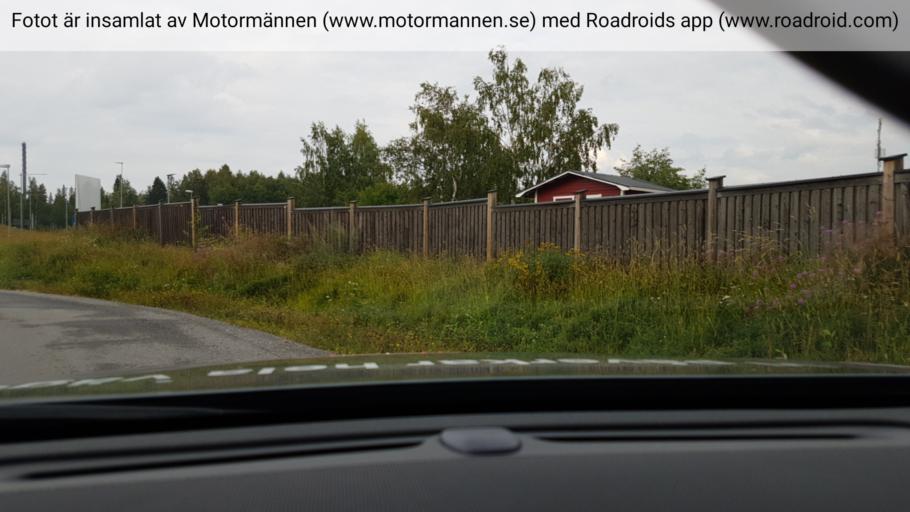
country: SE
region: Vaesterbotten
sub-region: Umea Kommun
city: Ersmark
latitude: 63.8443
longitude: 20.3416
